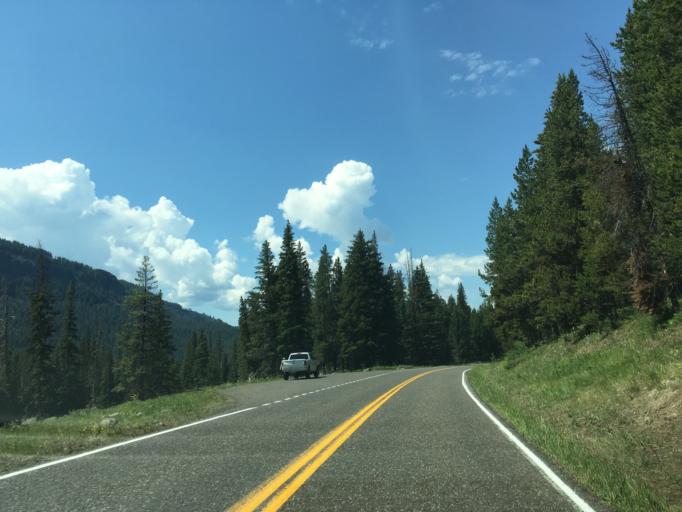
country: US
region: Montana
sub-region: Park County
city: Livingston
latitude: 44.9220
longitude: -110.0950
